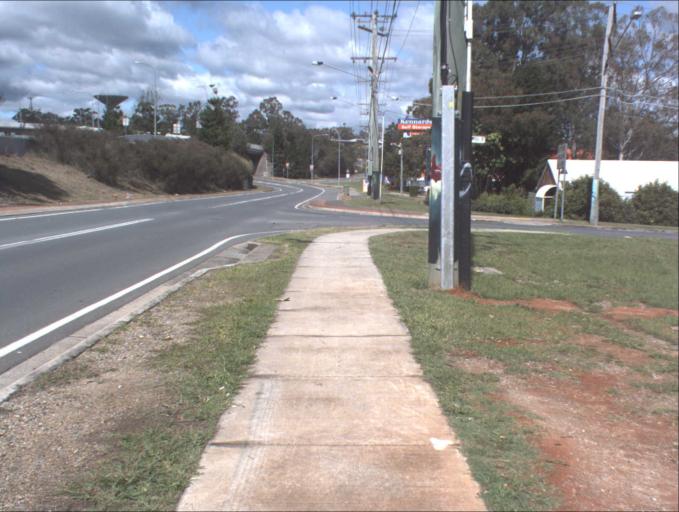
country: AU
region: Queensland
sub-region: Logan
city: Park Ridge South
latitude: -27.6718
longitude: 153.0312
